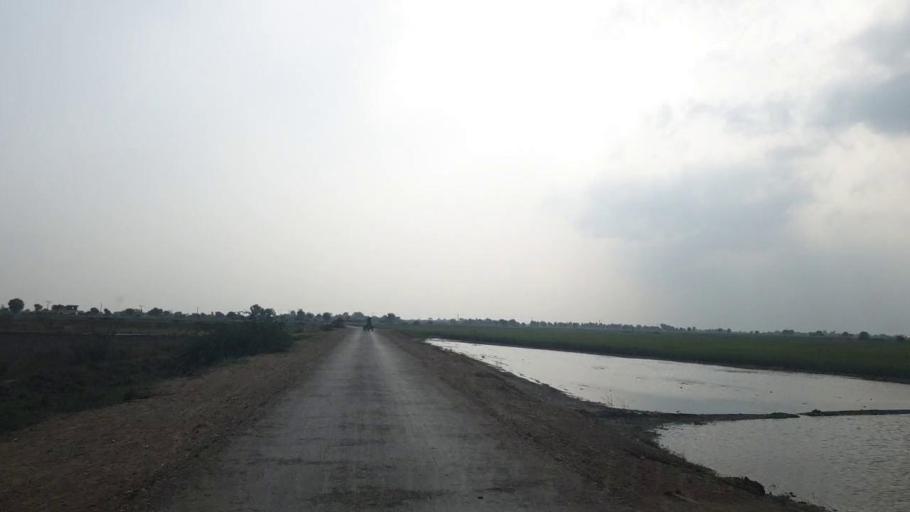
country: PK
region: Sindh
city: Badin
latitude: 24.6476
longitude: 68.6984
